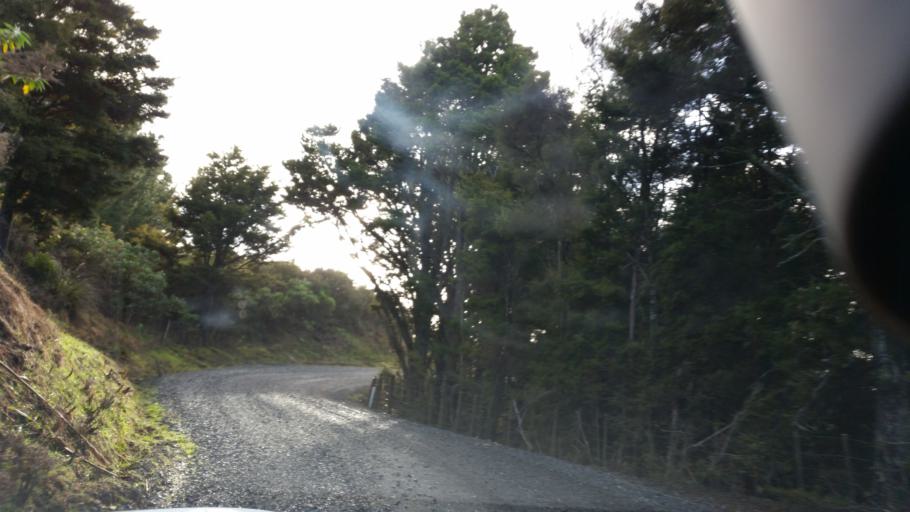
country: NZ
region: Northland
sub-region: Whangarei
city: Maungatapere
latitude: -35.7873
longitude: 174.0804
